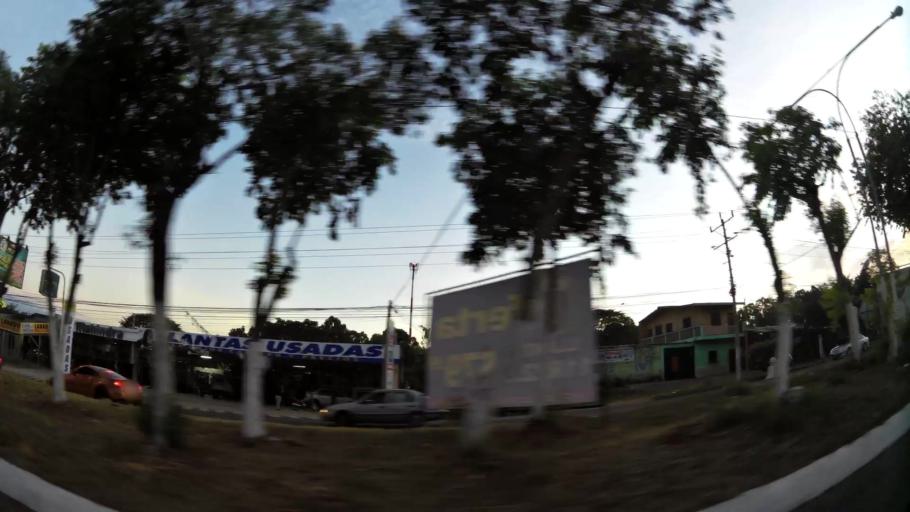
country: SV
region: Santa Ana
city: Santa Ana
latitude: 13.9852
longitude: -89.5491
